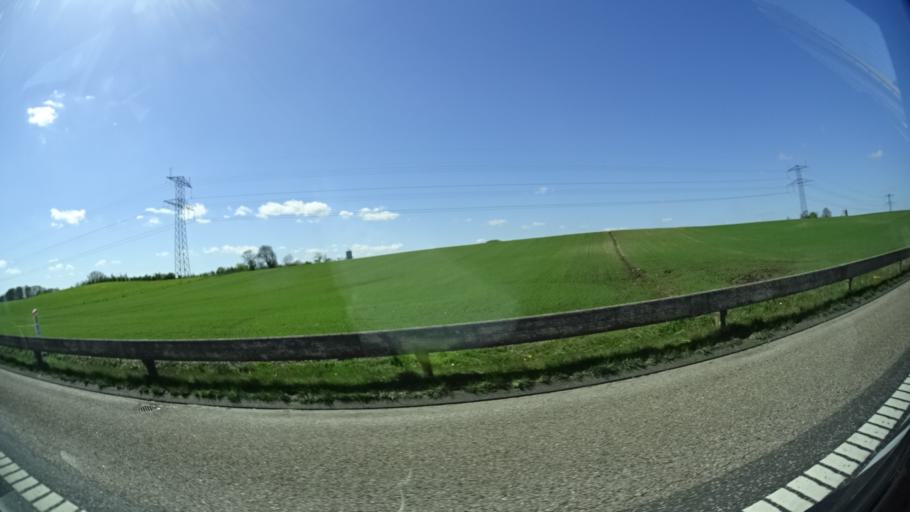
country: DK
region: Central Jutland
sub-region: Arhus Kommune
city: Trige
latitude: 56.2869
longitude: 10.1378
